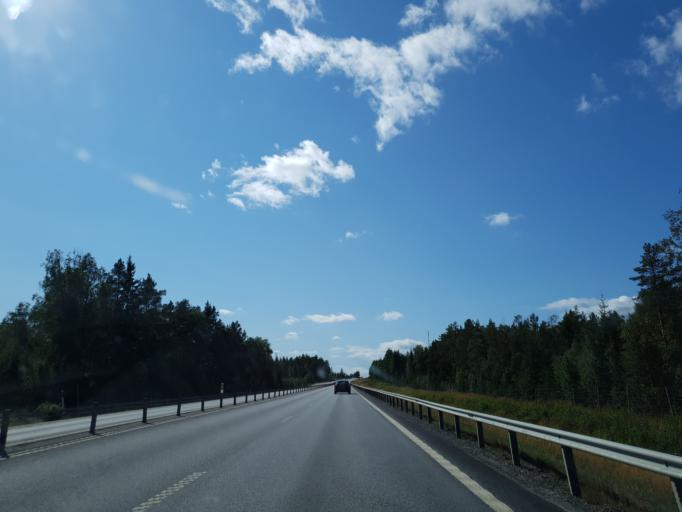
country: SE
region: Vaesterbotten
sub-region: Umea Kommun
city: Hoernefors
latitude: 63.6590
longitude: 19.9590
